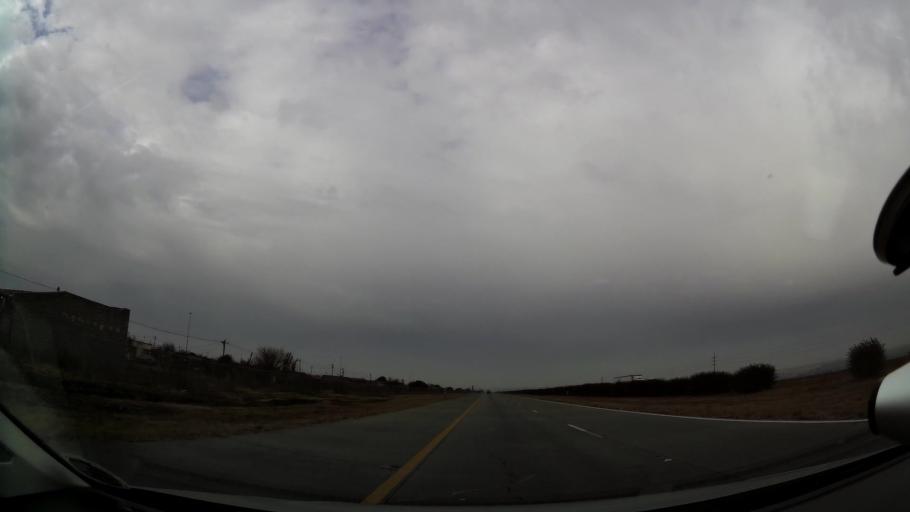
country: ZA
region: Gauteng
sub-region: City of Johannesburg Metropolitan Municipality
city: Orange Farm
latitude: -26.5121
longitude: 27.8118
